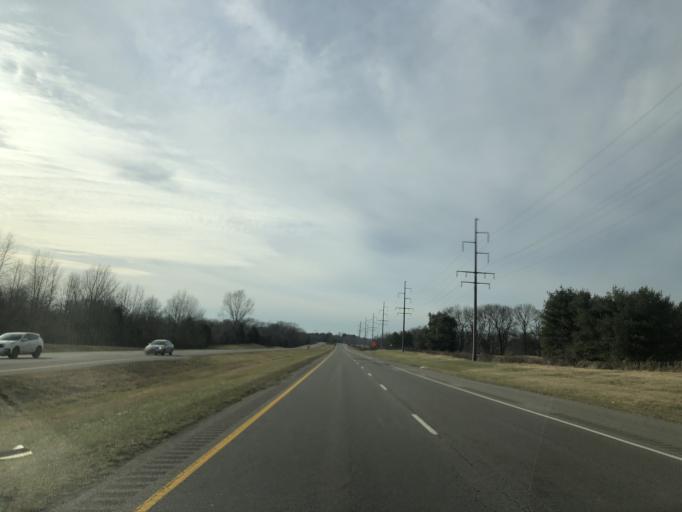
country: US
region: Tennessee
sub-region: Williamson County
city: Franklin
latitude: 35.9483
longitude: -86.8649
